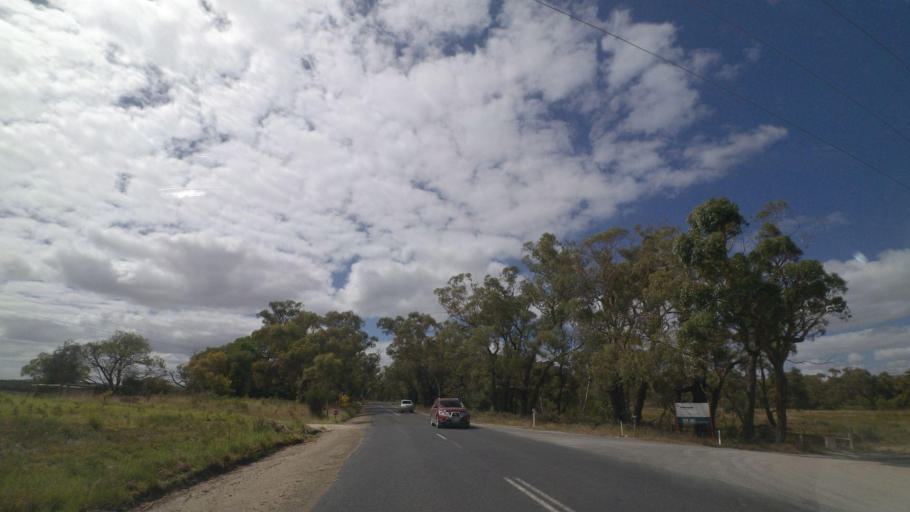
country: AU
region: Victoria
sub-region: Cardinia
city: Koo-Wee-Rup
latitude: -38.2895
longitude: 145.6201
